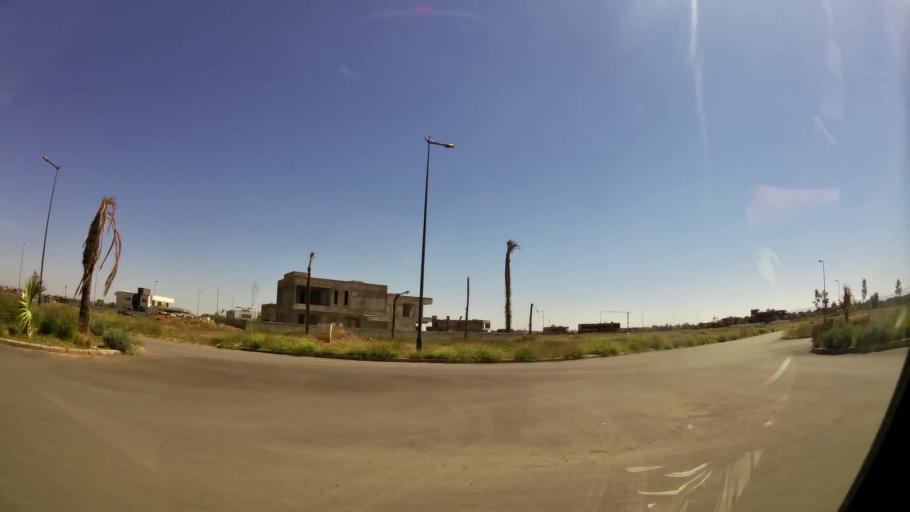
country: MA
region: Marrakech-Tensift-Al Haouz
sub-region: Marrakech
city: Marrakesh
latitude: 31.5928
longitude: -8.0033
